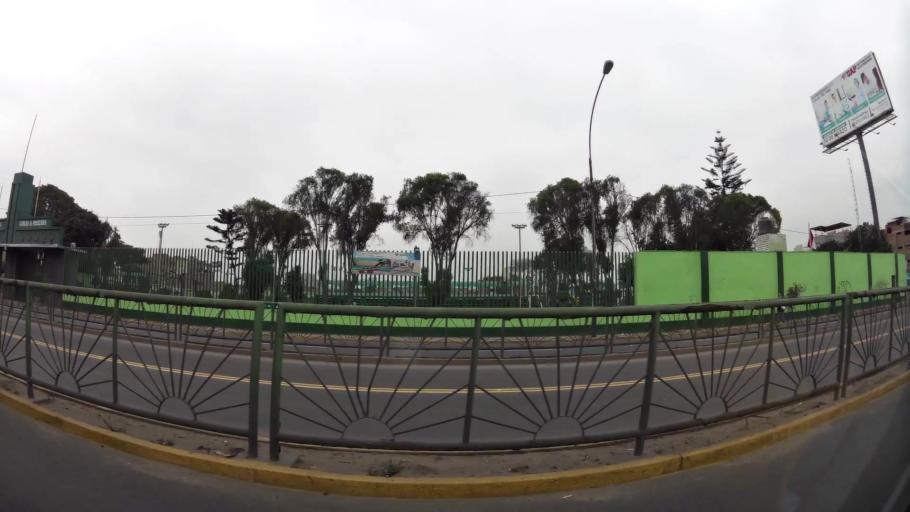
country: PE
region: Lima
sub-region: Lima
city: Surco
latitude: -12.1150
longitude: -77.0106
